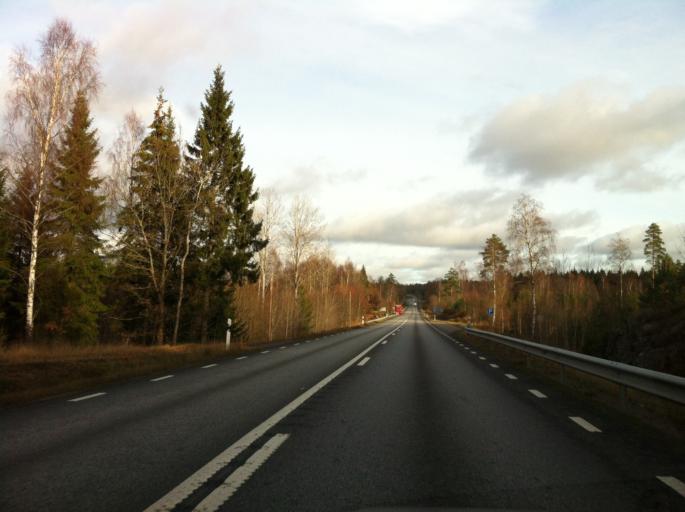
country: SE
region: Kronoberg
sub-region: Alvesta Kommun
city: Vislanda
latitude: 56.7735
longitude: 14.5421
